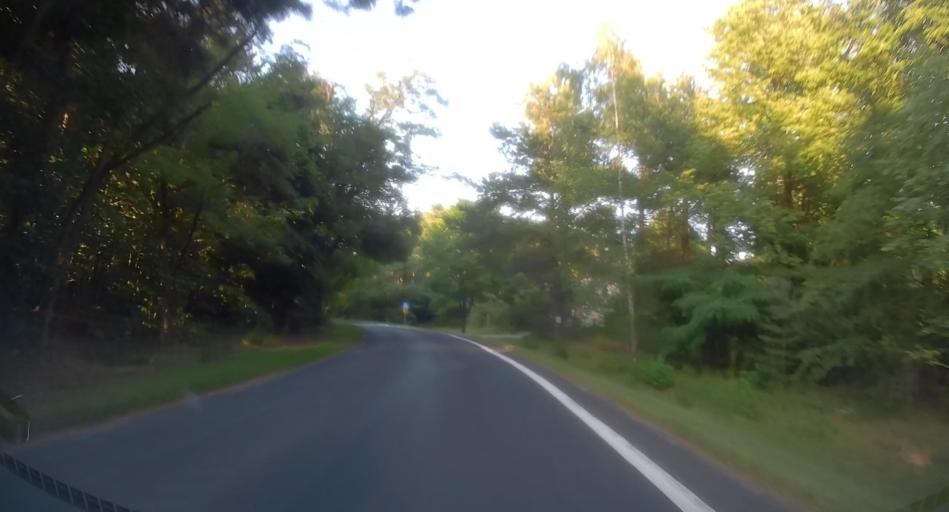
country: PL
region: Masovian Voivodeship
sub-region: Powiat zyrardowski
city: Puszcza Marianska
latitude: 51.9069
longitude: 20.3416
